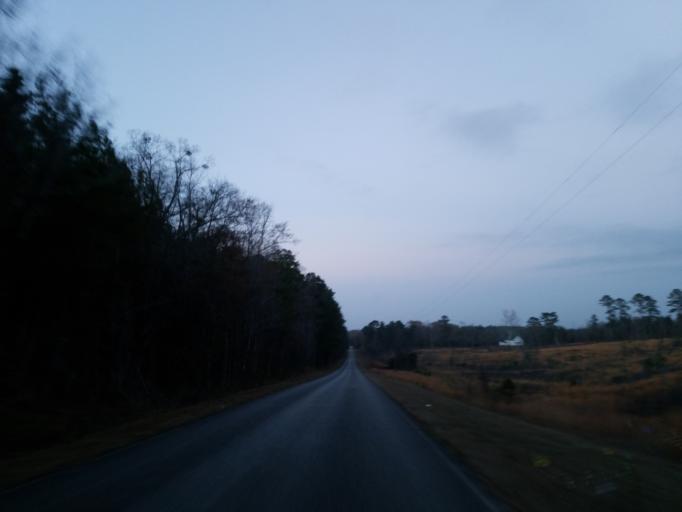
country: US
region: Alabama
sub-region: Sumter County
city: York
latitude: 32.4157
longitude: -88.4384
